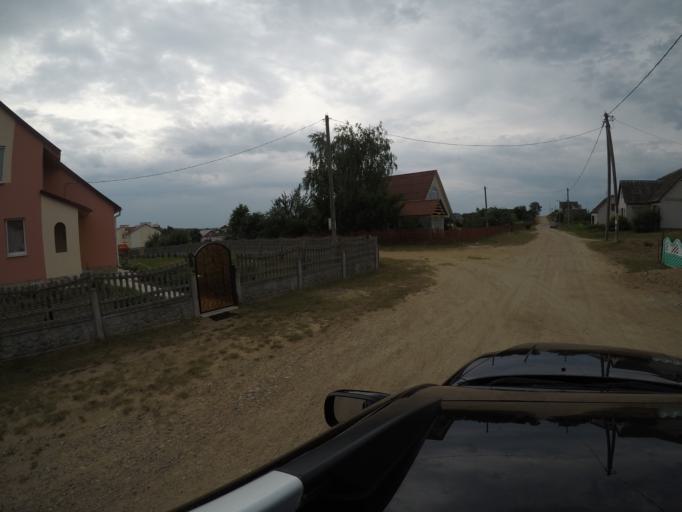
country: BY
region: Grodnenskaya
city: Hal'shany
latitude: 54.2593
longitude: 26.0231
